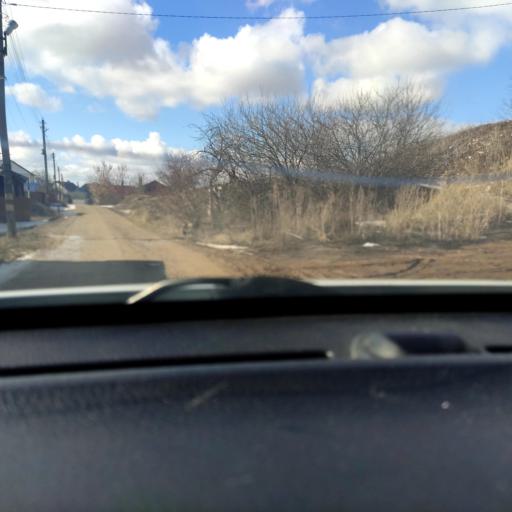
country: RU
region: Voronezj
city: Somovo
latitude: 51.6904
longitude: 39.3826
